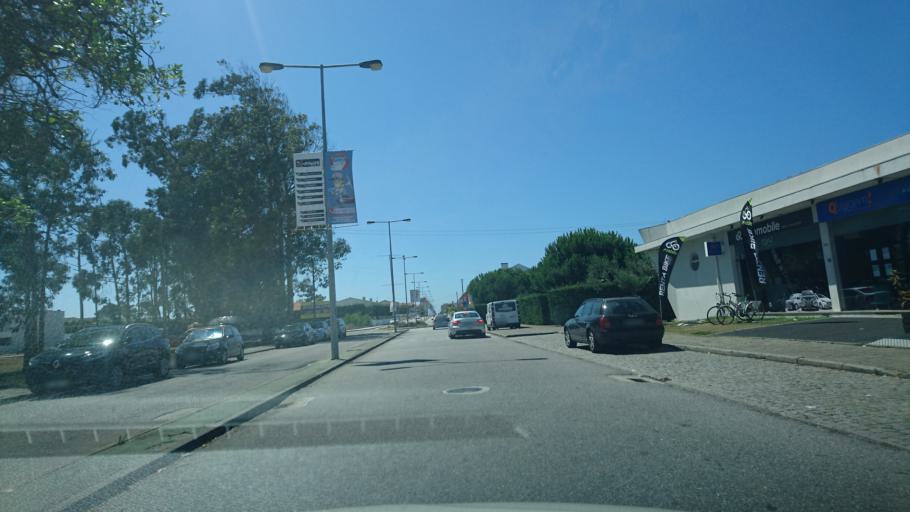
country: PT
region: Aveiro
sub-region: Ovar
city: Esmoriz
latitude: 40.9569
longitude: -8.6450
